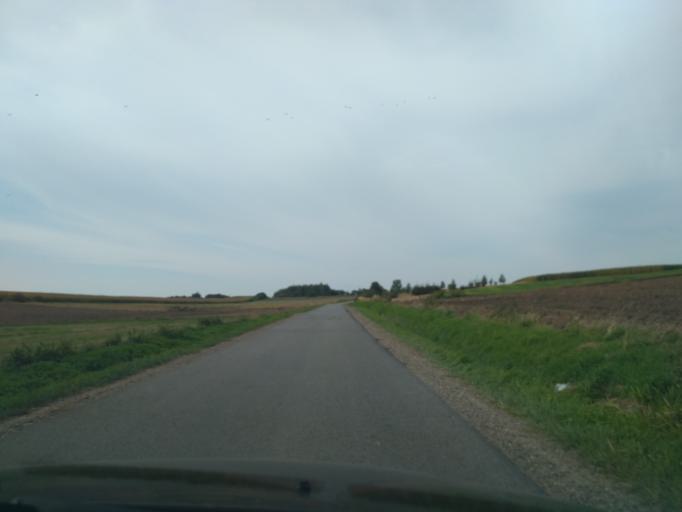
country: PL
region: Subcarpathian Voivodeship
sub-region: Powiat rzeszowski
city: Zglobien
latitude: 50.0216
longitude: 21.8459
